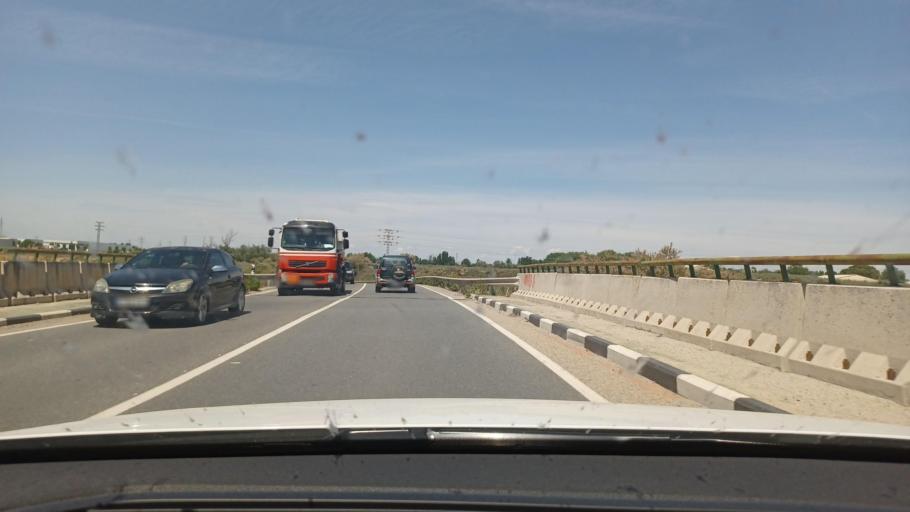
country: ES
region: Madrid
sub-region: Provincia de Madrid
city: Meco
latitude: 40.5361
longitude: -3.2963
